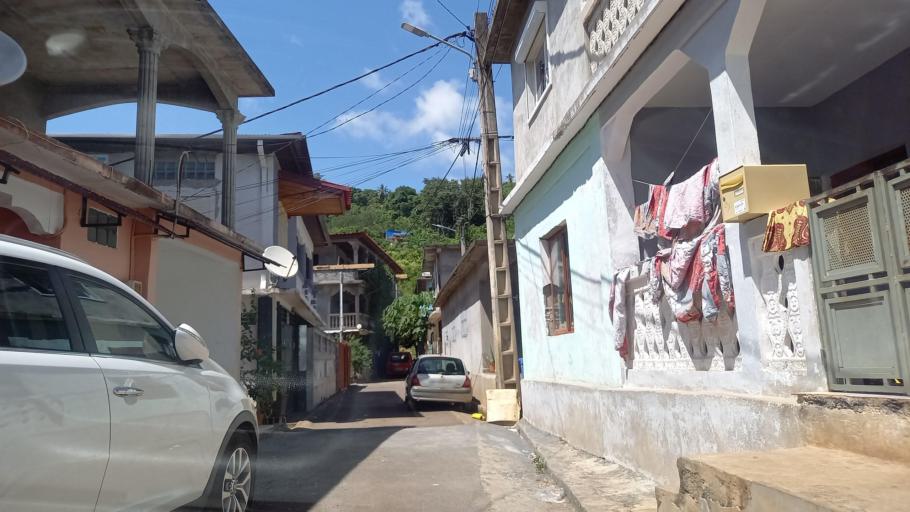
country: YT
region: Bandraboua
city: Bandraboua
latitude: -12.6829
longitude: 45.1012
